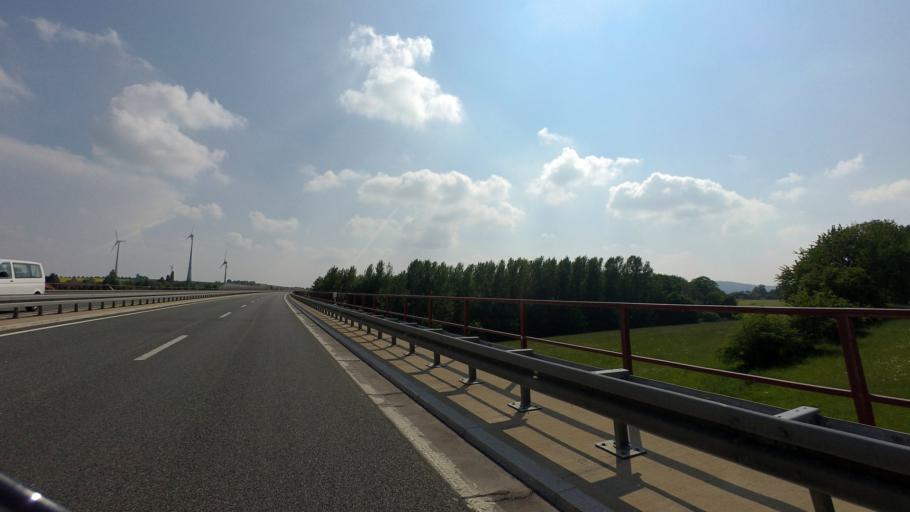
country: DE
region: Saxony
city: Lobau
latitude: 51.1399
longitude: 14.6535
